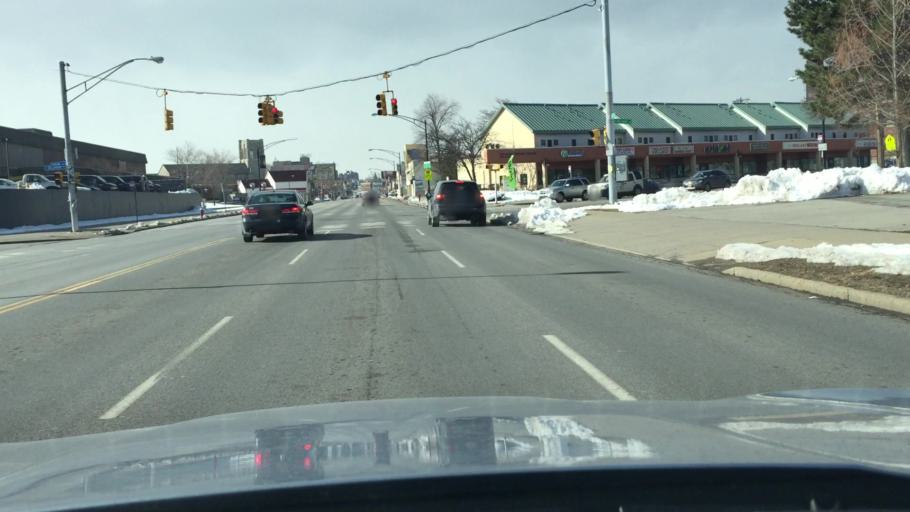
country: US
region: New York
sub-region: Erie County
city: Buffalo
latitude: 42.9225
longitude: -78.8570
